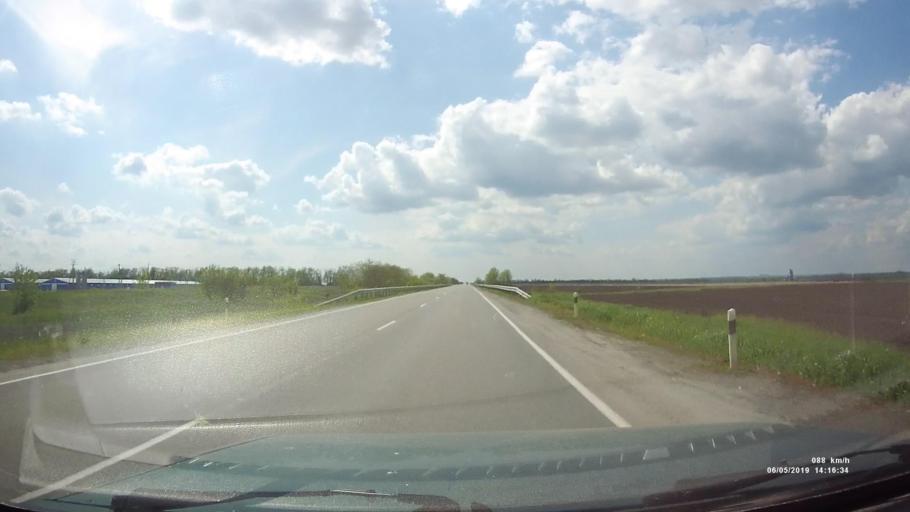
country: RU
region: Rostov
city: Kamenolomni
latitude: 47.6347
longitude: 40.2852
